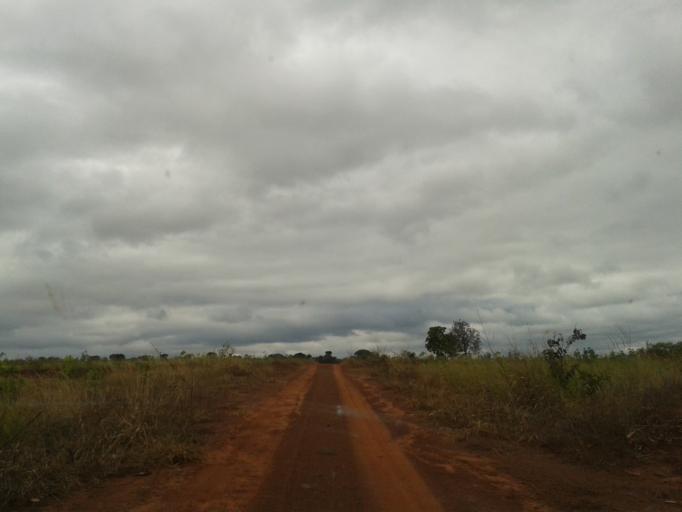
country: BR
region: Minas Gerais
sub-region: Campina Verde
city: Campina Verde
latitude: -19.5103
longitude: -49.6349
